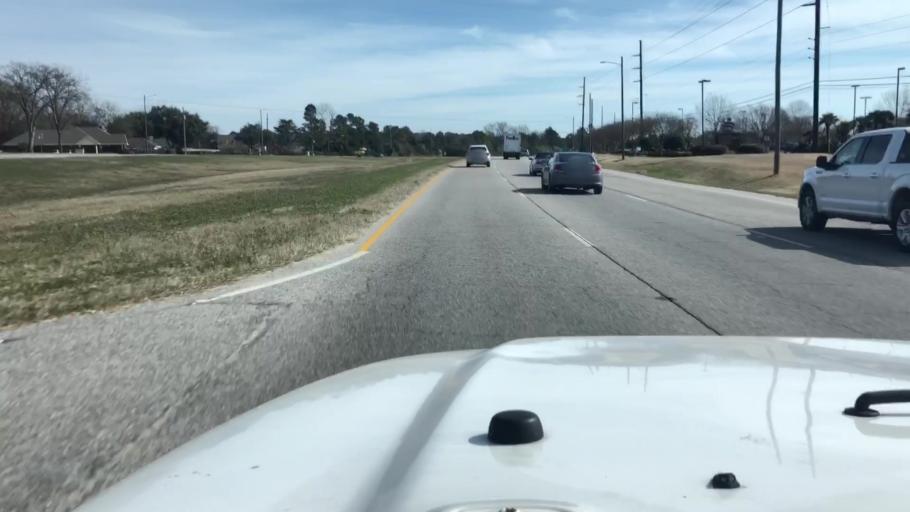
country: US
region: Alabama
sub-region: Elmore County
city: Blue Ridge
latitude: 32.3820
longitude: -86.1642
